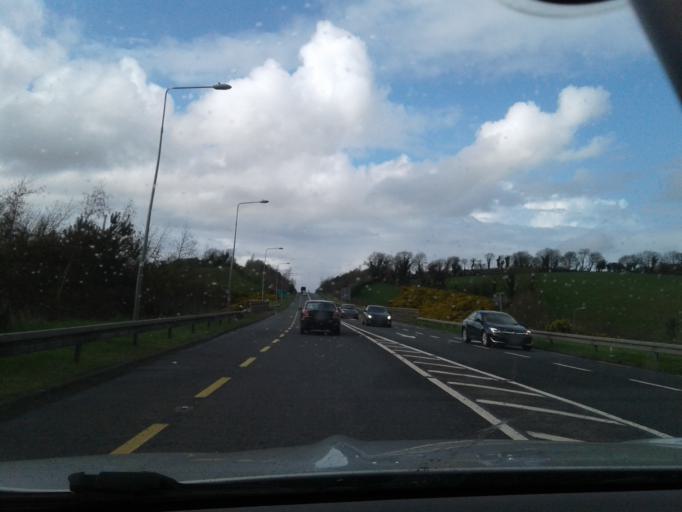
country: IE
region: Ulster
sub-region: County Monaghan
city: Carrickmacross
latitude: 53.9714
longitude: -6.6984
